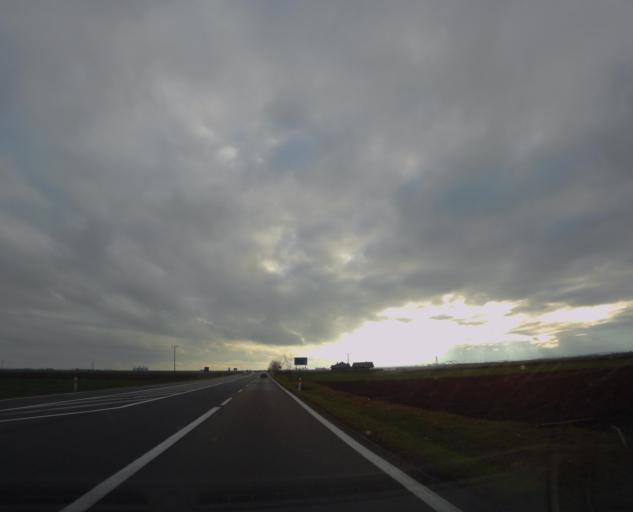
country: PL
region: Subcarpathian Voivodeship
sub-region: Powiat jaroslawski
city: Radymno
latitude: 49.9209
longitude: 22.8204
